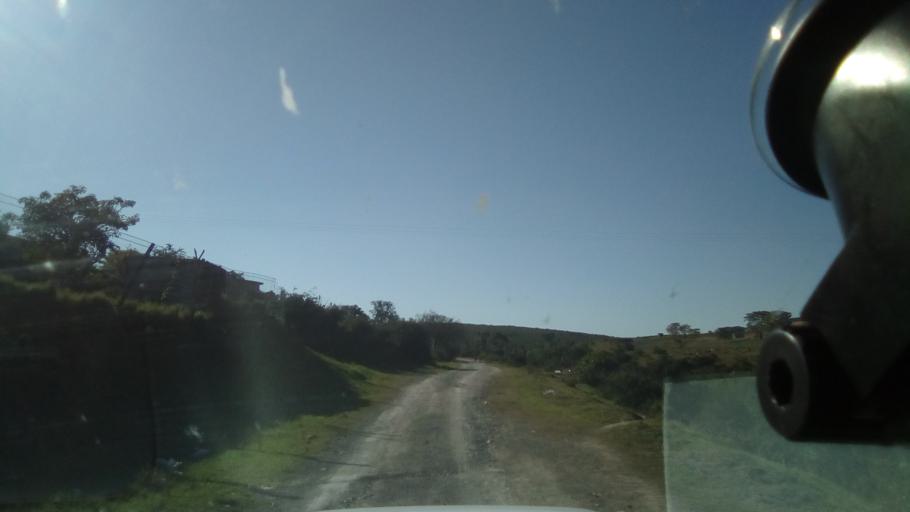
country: ZA
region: Eastern Cape
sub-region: Buffalo City Metropolitan Municipality
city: Bhisho
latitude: -32.7995
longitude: 27.3415
